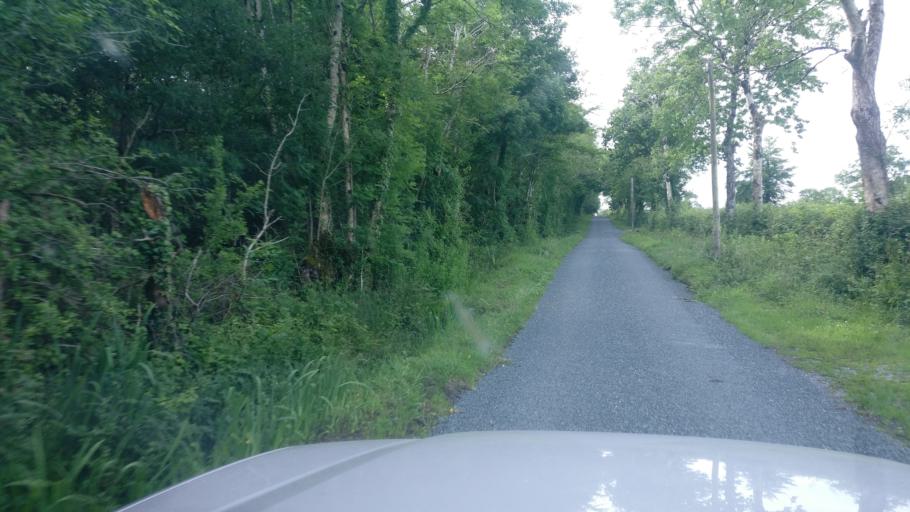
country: IE
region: Connaught
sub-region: County Galway
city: Gort
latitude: 53.1038
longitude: -8.7124
